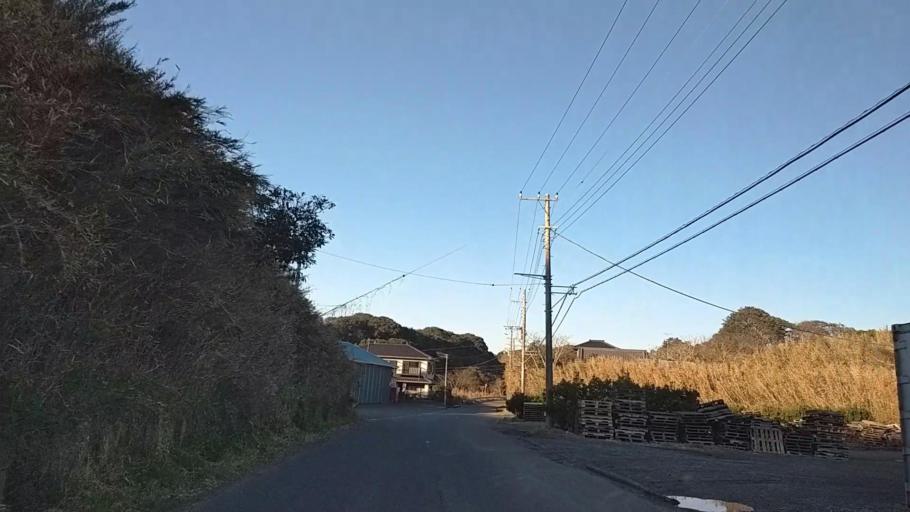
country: JP
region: Chiba
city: Asahi
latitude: 35.7095
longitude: 140.7280
